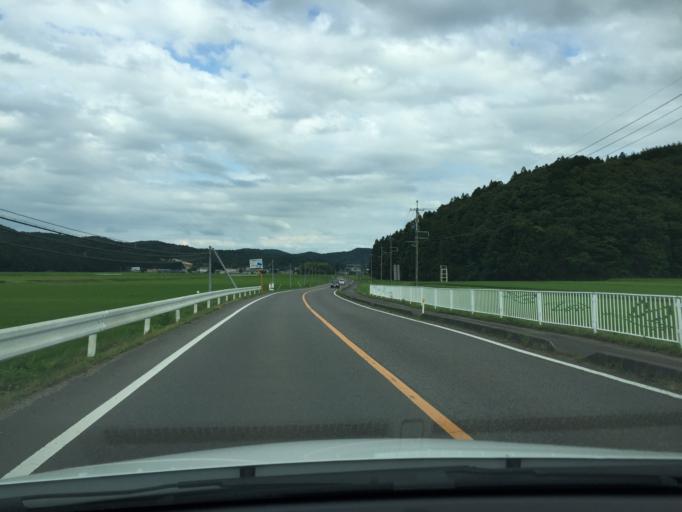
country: JP
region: Tochigi
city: Kuroiso
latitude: 37.1737
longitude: 140.1601
